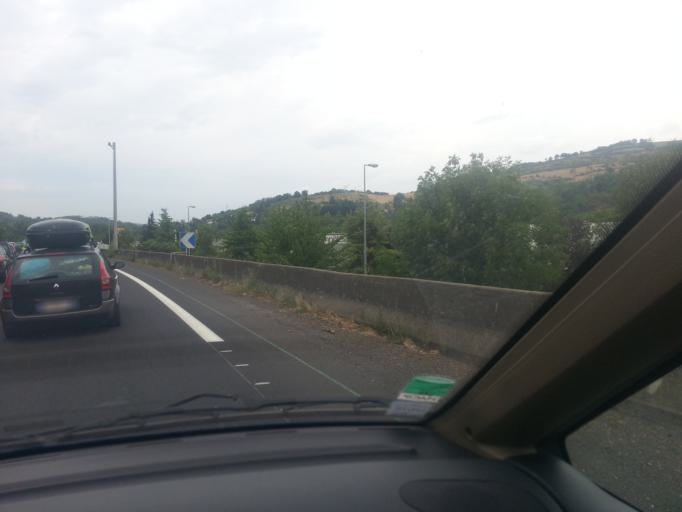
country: FR
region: Auvergne
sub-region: Departement du Puy-de-Dome
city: Vic-le-Comte
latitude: 45.6089
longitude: 3.2213
